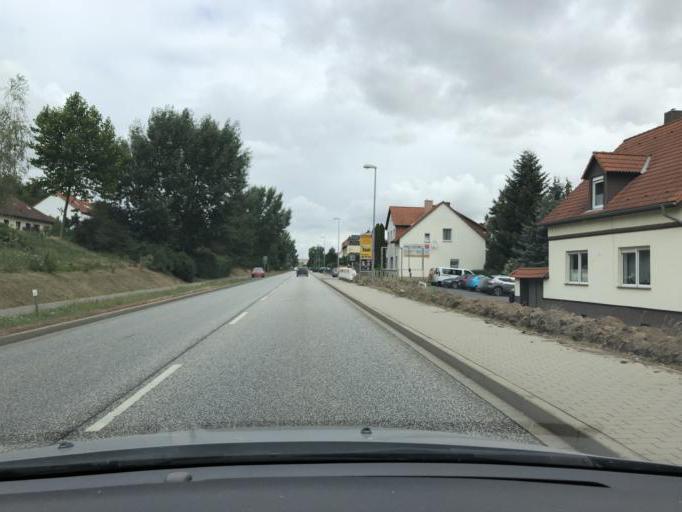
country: DE
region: Saxony-Anhalt
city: Volkstedt
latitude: 51.5174
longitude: 11.5631
